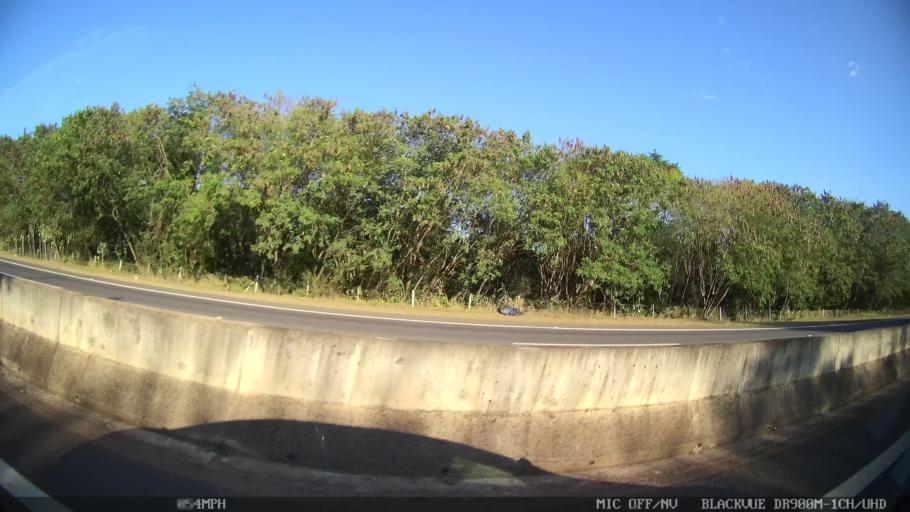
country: BR
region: Sao Paulo
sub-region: Piracicaba
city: Piracicaba
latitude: -22.7010
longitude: -47.6425
